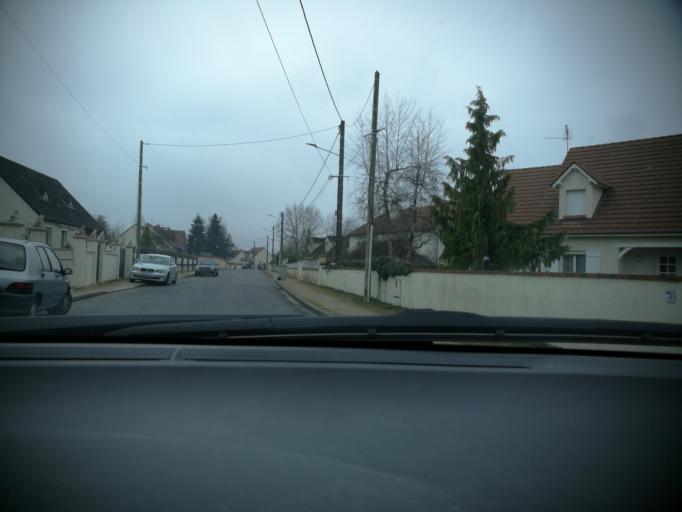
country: FR
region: Centre
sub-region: Departement du Loiret
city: Semoy
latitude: 47.9269
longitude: 1.9450
